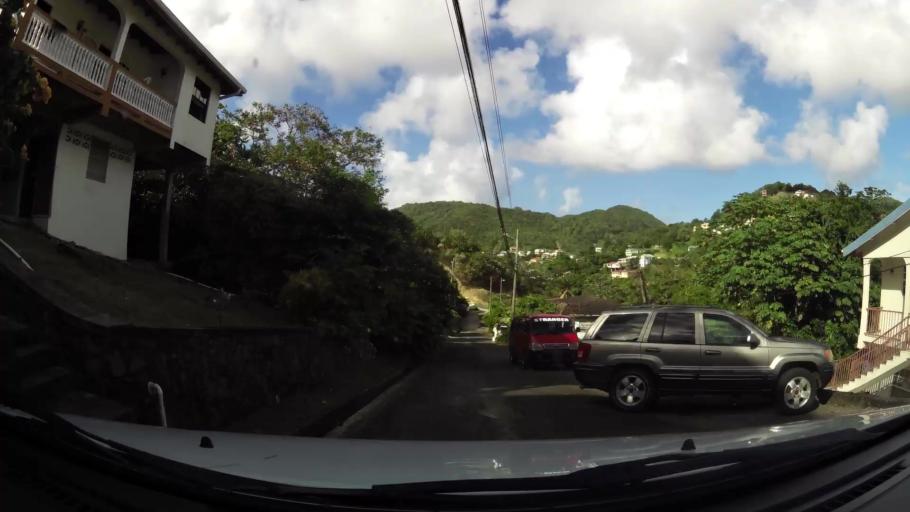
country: LC
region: Castries Quarter
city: Bisee
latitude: 14.0394
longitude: -60.9562
